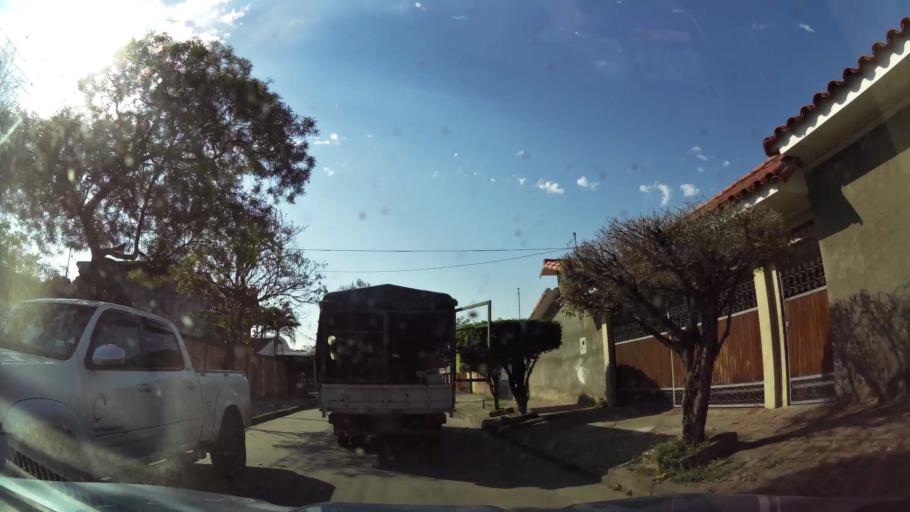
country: BO
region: Santa Cruz
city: Santa Cruz de la Sierra
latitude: -17.7840
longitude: -63.1614
